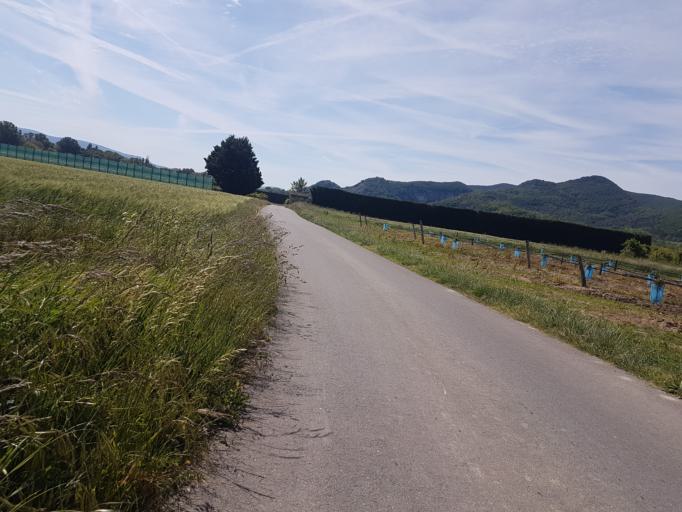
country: FR
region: Rhone-Alpes
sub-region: Departement de l'Ardeche
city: Le Pouzin
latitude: 44.7278
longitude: 4.7560
